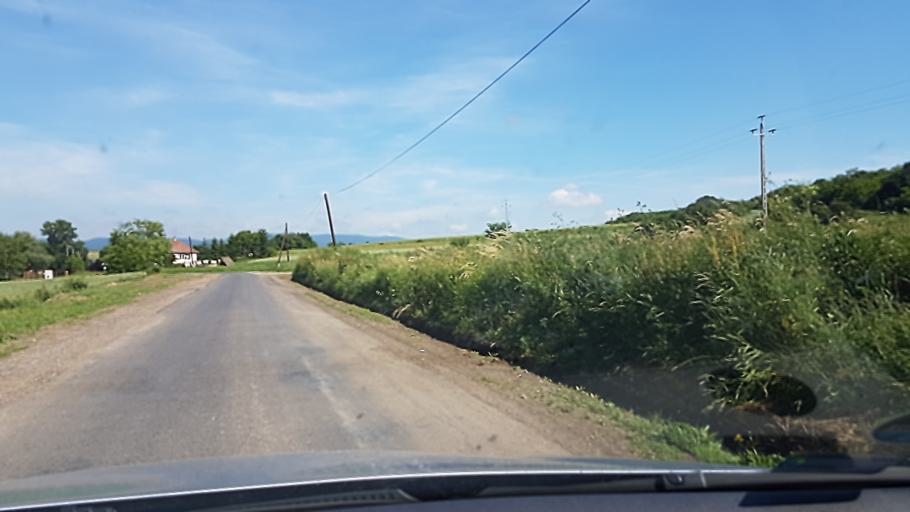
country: HU
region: Borsod-Abauj-Zemplen
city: Saly
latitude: 47.9500
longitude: 20.7001
